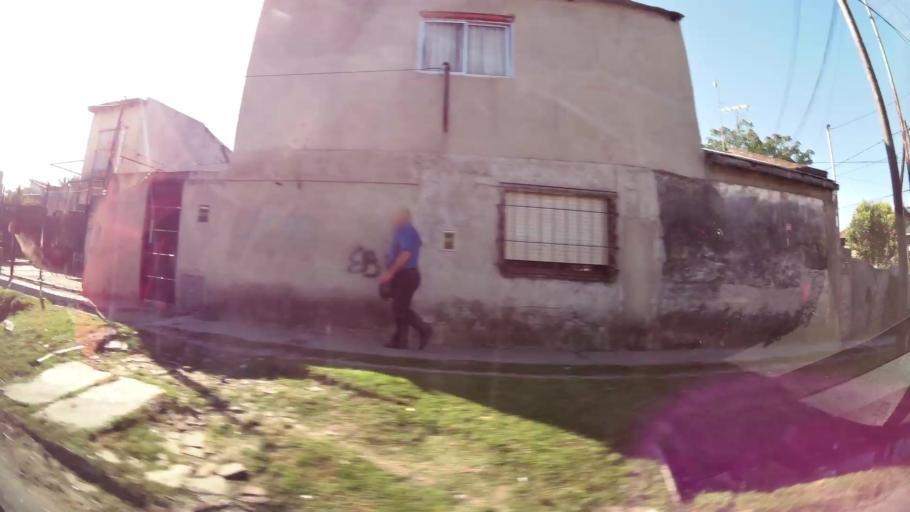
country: AR
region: Buenos Aires
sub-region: Partido de Tigre
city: Tigre
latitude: -34.4883
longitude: -58.6603
